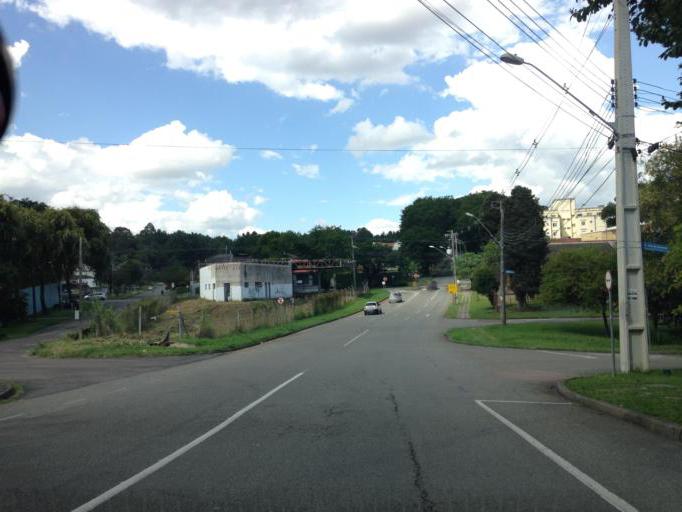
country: BR
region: Parana
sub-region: Curitiba
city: Curitiba
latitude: -25.4111
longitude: -49.2373
